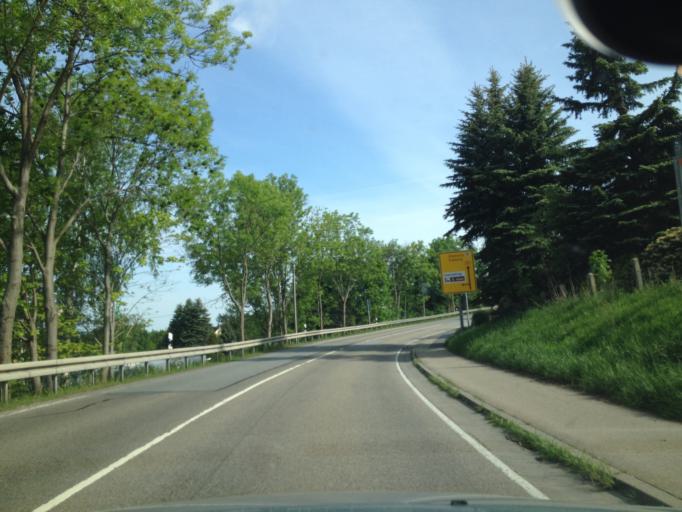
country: DE
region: Saxony
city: Annaberg-Buchholz
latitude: 50.5723
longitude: 13.0099
